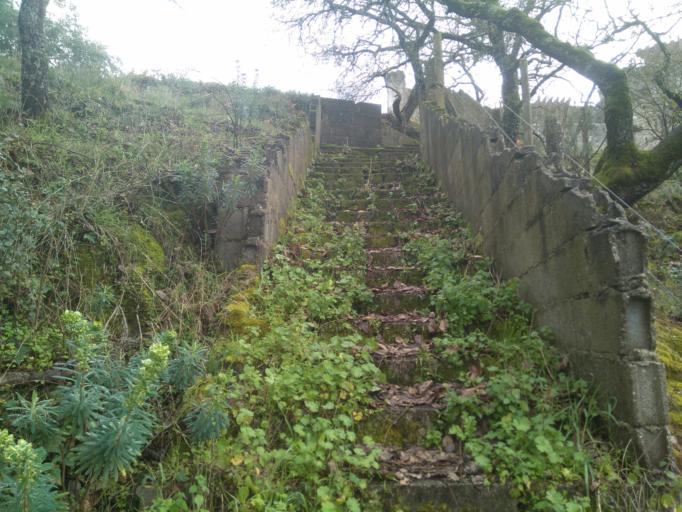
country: PT
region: Leiria
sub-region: Porto de Mos
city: Porto de Mos
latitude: 39.6043
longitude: -8.8183
